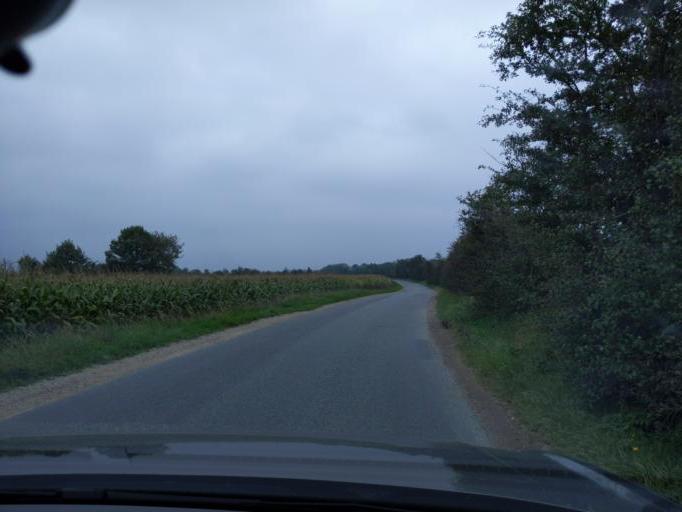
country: DK
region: Central Jutland
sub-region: Viborg Kommune
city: Stoholm
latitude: 56.5094
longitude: 9.2536
